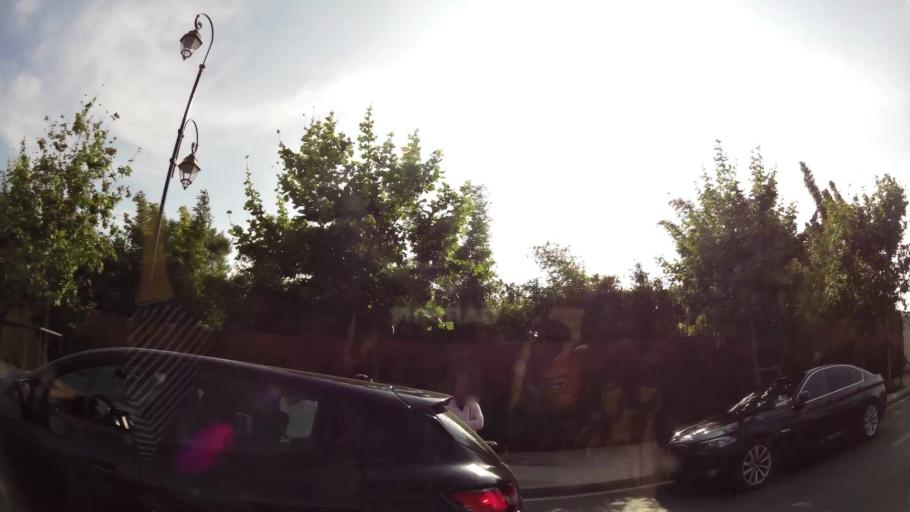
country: MA
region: Rabat-Sale-Zemmour-Zaer
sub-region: Rabat
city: Rabat
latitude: 33.9590
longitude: -6.8187
